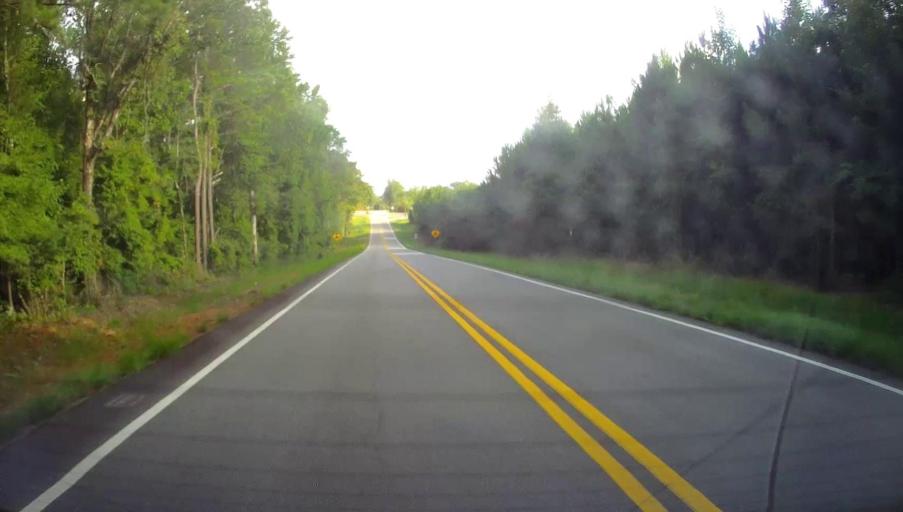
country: US
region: Georgia
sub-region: Crawford County
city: Knoxville
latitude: 32.8783
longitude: -83.9955
